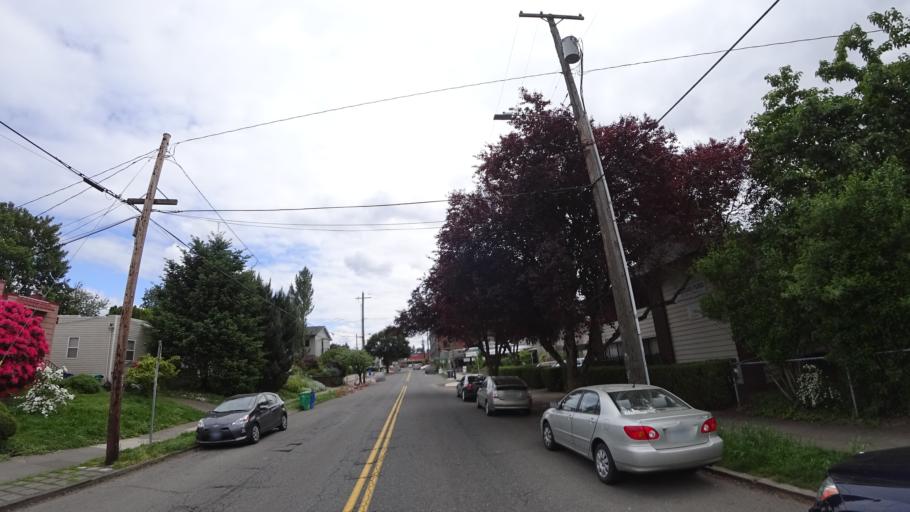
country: US
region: Oregon
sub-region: Multnomah County
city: Lents
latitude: 45.5071
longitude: -122.6113
